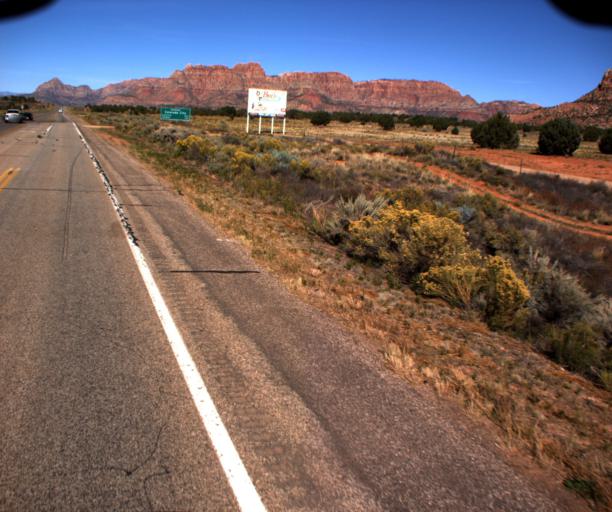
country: US
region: Arizona
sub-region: Mohave County
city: Colorado City
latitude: 36.9612
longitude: -112.9675
